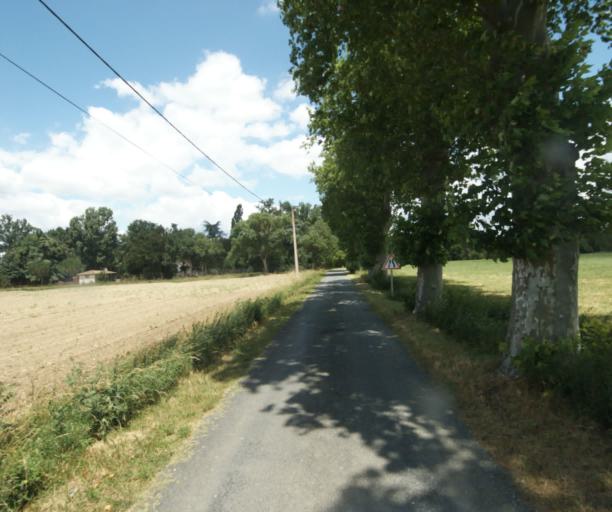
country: FR
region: Midi-Pyrenees
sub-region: Departement du Tarn
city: Puylaurens
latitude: 43.5188
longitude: 2.0215
